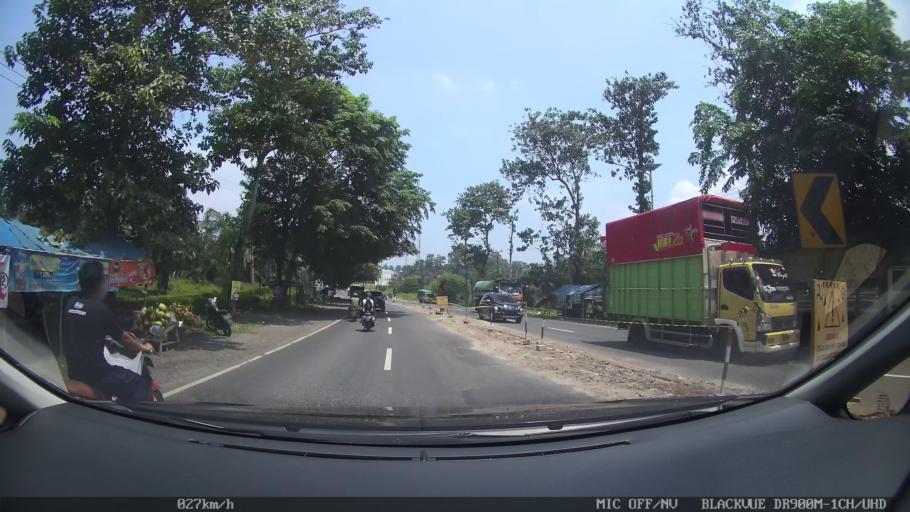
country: ID
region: Lampung
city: Natar
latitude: -5.3343
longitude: 105.2095
